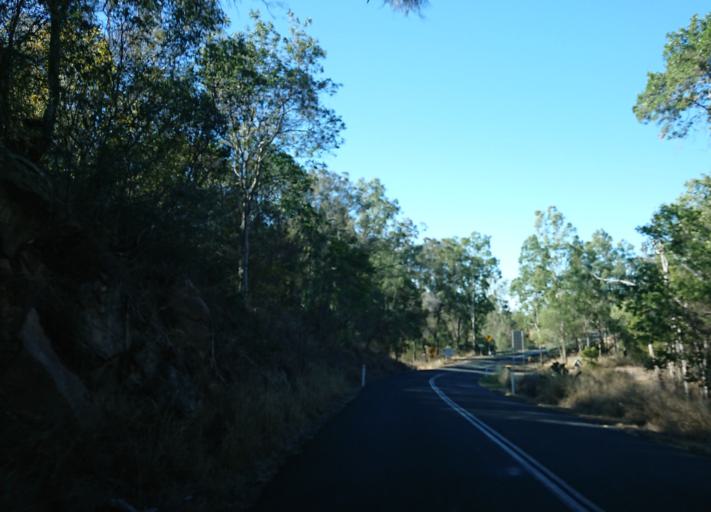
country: AU
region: Queensland
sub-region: Toowoomba
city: Top Camp
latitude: -27.7354
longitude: 152.1046
